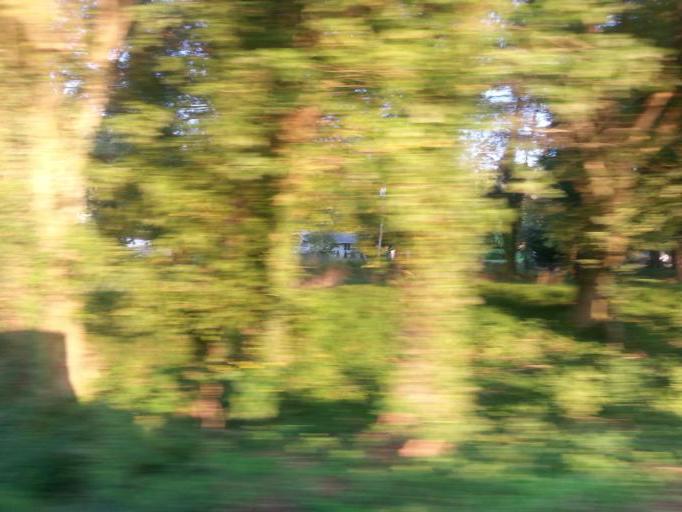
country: US
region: Tennessee
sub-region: Roane County
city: Kingston
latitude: 35.8658
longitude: -84.5226
